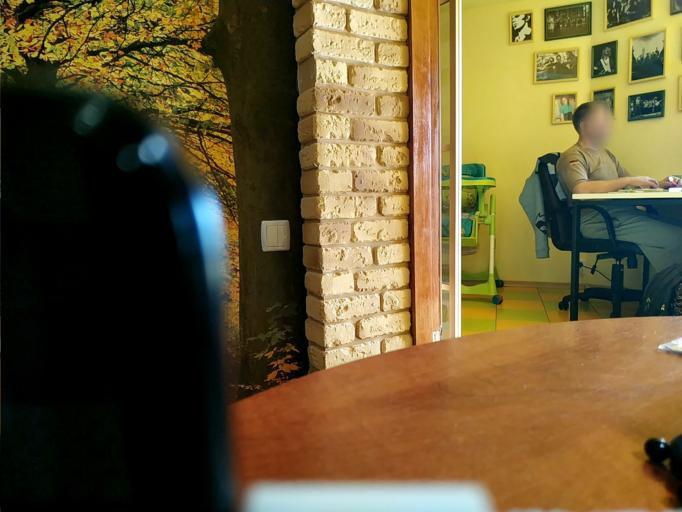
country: RU
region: Tverskaya
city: Vasil'yevskiy Mokh
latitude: 57.1264
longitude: 35.8675
